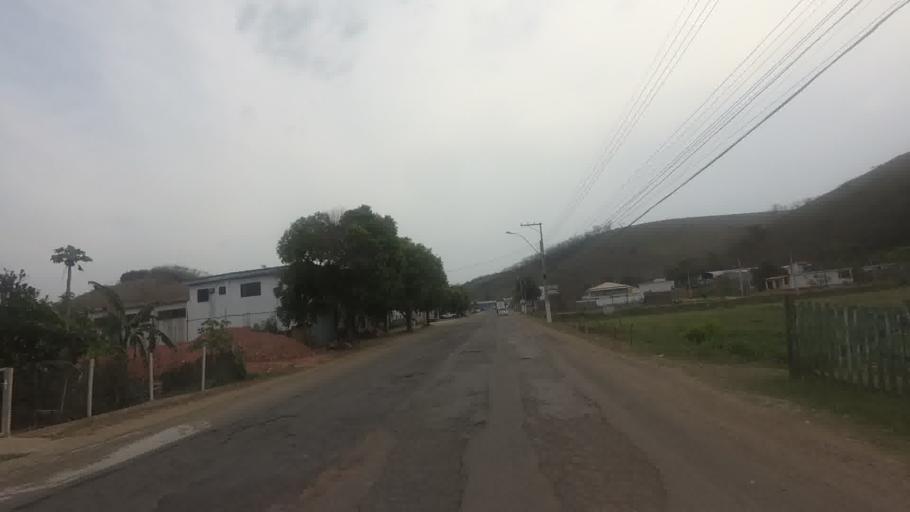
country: BR
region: Rio de Janeiro
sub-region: Santo Antonio De Padua
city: Santo Antonio de Padua
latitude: -21.5394
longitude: -42.1620
